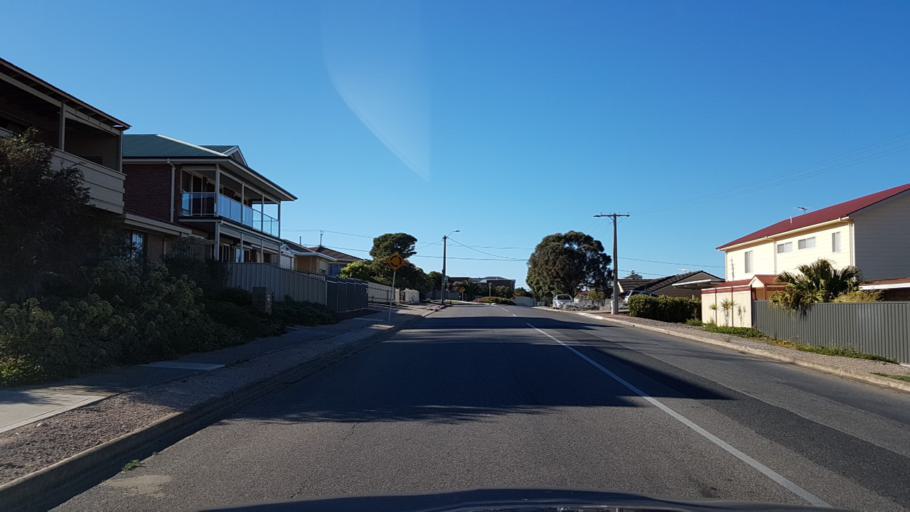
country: AU
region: South Australia
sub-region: Adelaide
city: Port Noarlunga
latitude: -35.1342
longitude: 138.4733
